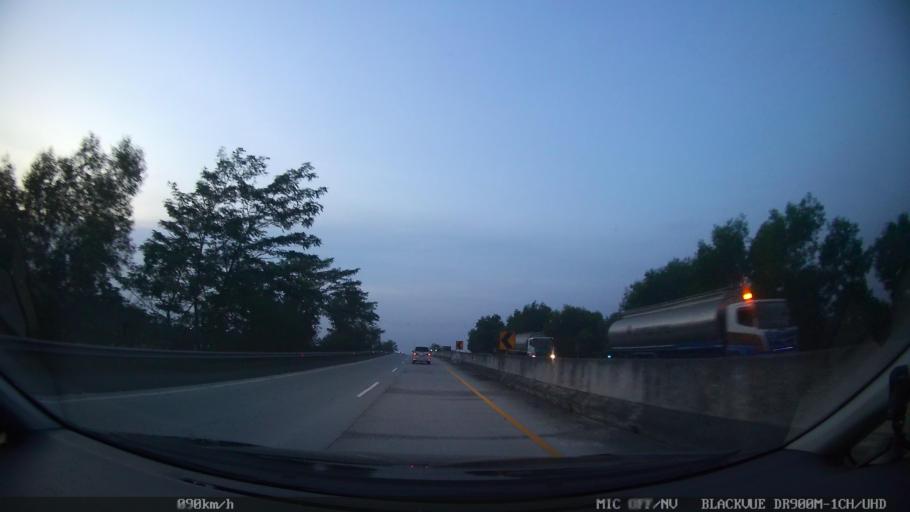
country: ID
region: Lampung
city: Sidorejo
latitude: -5.6028
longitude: 105.5543
